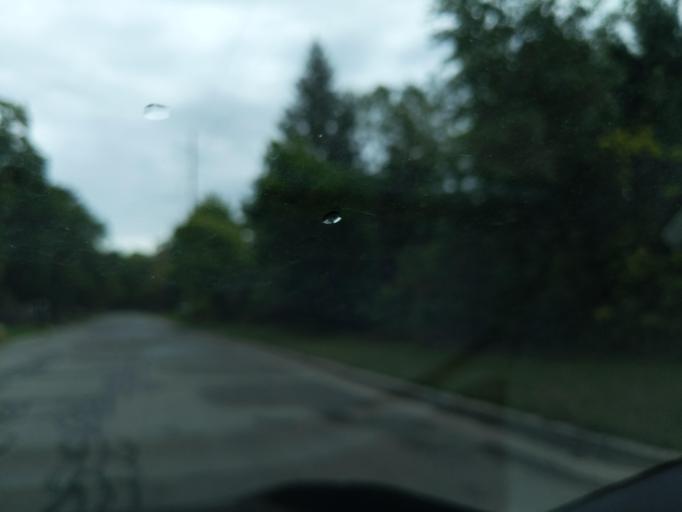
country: US
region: Michigan
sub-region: Grand Traverse County
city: Traverse City
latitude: 44.7551
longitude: -85.5926
